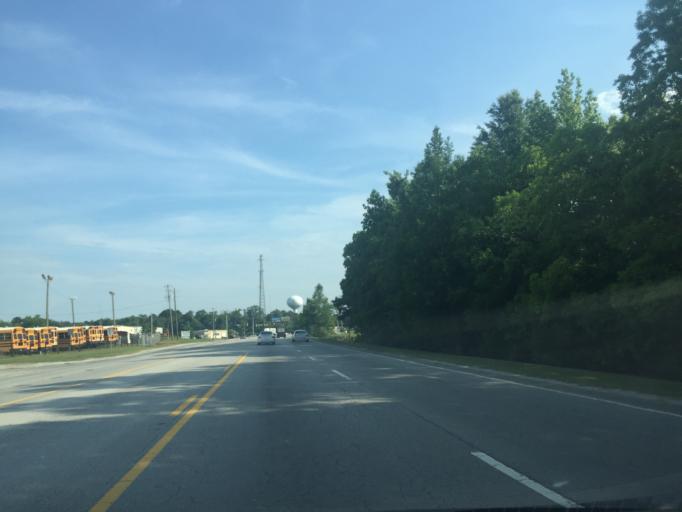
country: US
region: Georgia
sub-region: Chatham County
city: Garden City
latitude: 32.0824
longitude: -81.1576
